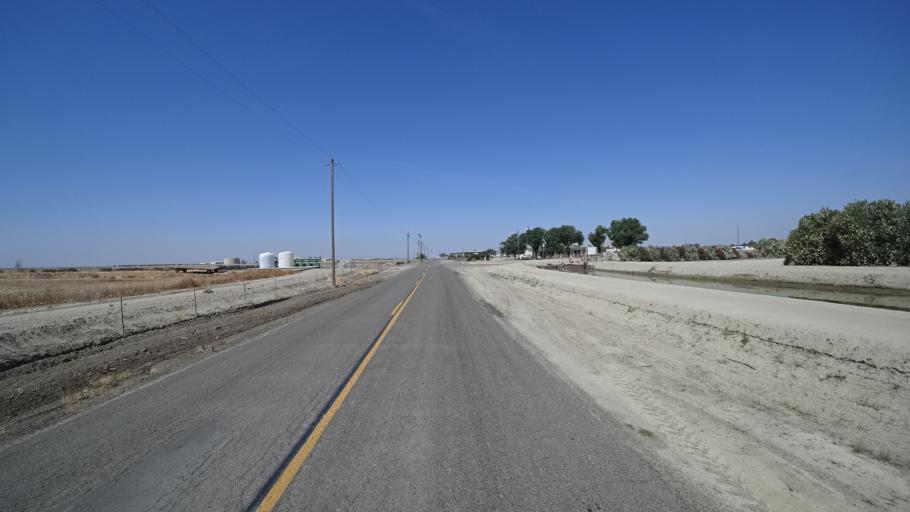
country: US
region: California
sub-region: Kings County
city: Corcoran
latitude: 36.0726
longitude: -119.5534
